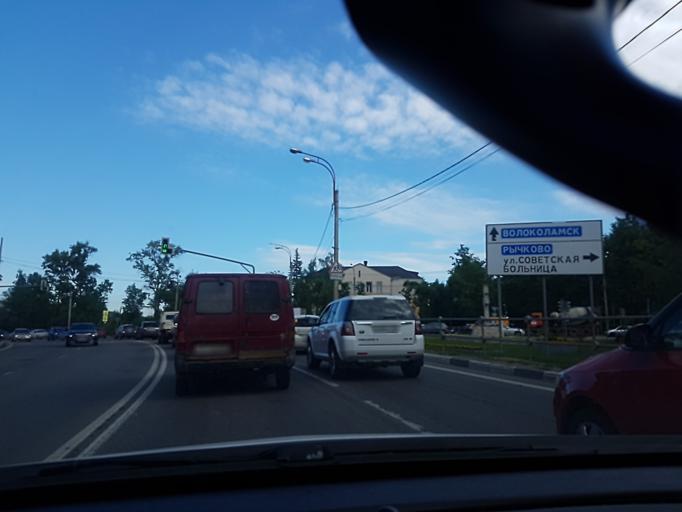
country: RU
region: Moskovskaya
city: Istra
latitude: 55.9197
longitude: 36.8590
